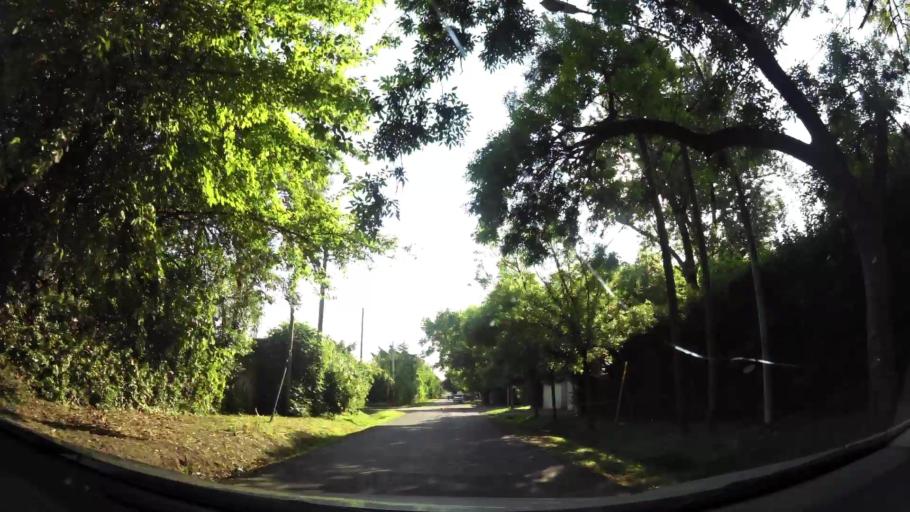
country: AR
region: Buenos Aires
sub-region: Partido de Tigre
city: Tigre
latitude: -34.4734
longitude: -58.6371
